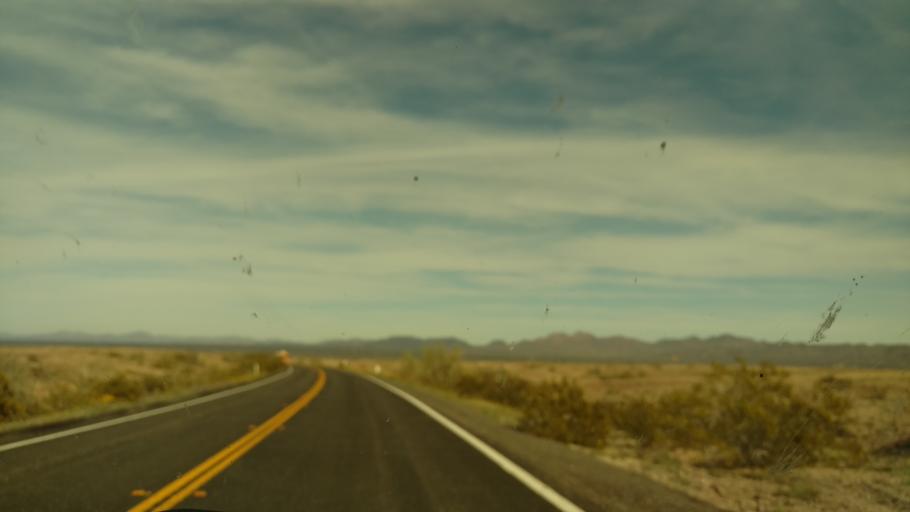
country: US
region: California
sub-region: Riverside County
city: Mesa Verde
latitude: 33.2895
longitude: -114.7580
